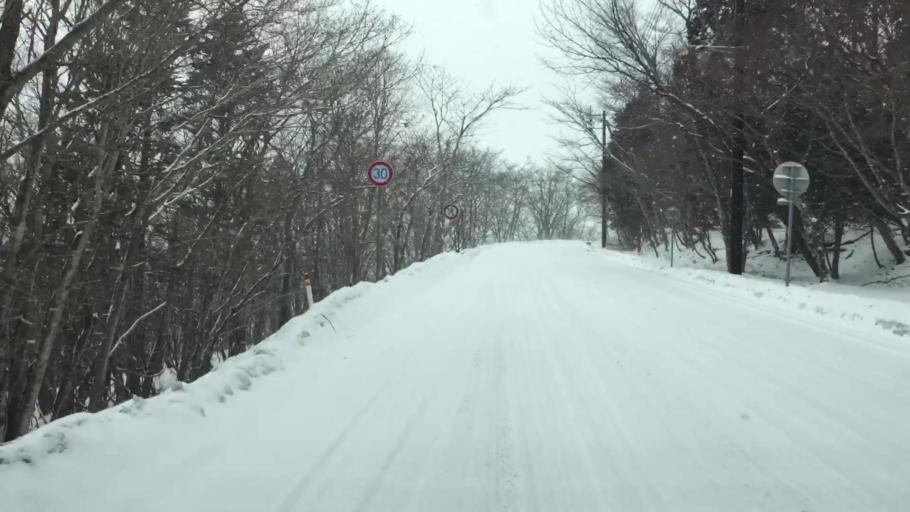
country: JP
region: Tochigi
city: Nikko
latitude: 36.9086
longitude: 139.7370
